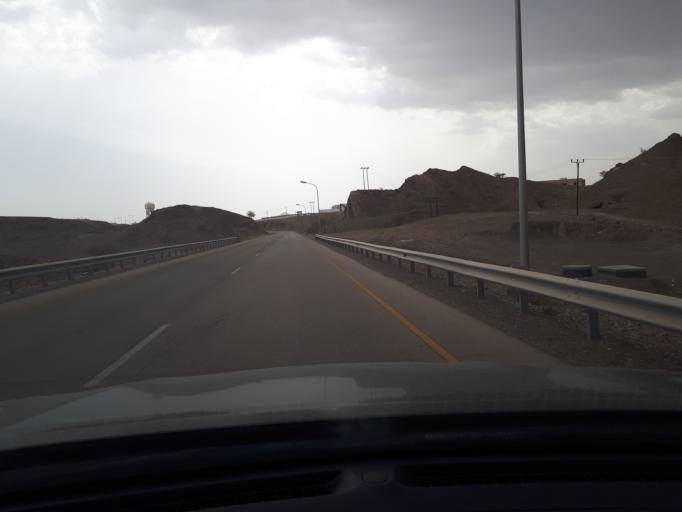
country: OM
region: Ash Sharqiyah
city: Badiyah
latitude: 22.5666
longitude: 59.0494
